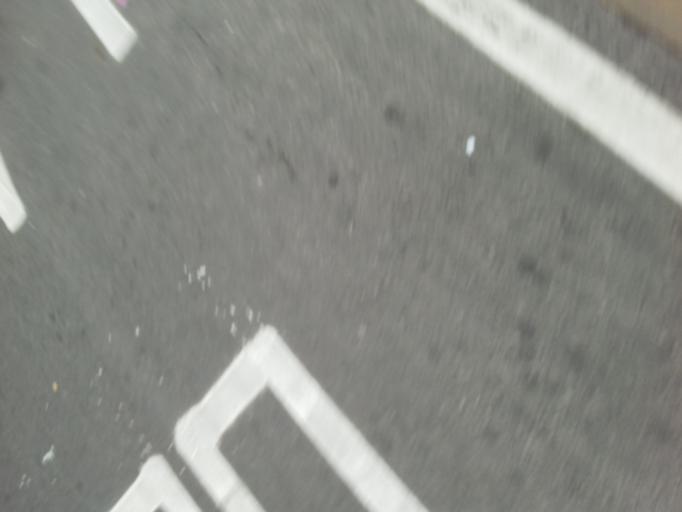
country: LK
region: Western
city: Colombo
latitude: 6.8942
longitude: 79.8552
